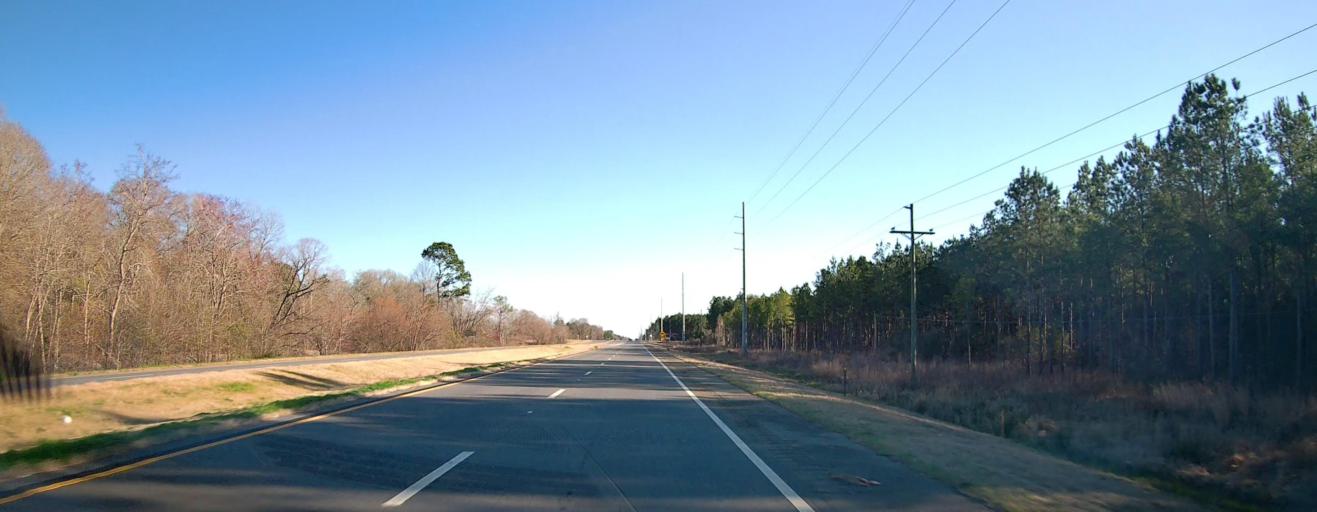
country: US
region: Georgia
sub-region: Lee County
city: Leesburg
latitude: 31.8791
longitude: -84.2421
